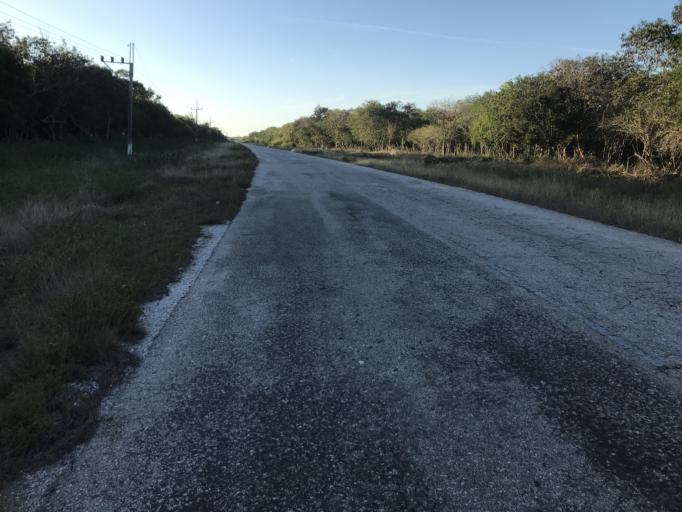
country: CU
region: Cienfuegos
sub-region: Municipio de Aguada de Pasajeros
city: Aguada de Pasajeros
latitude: 22.0759
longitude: -81.0617
